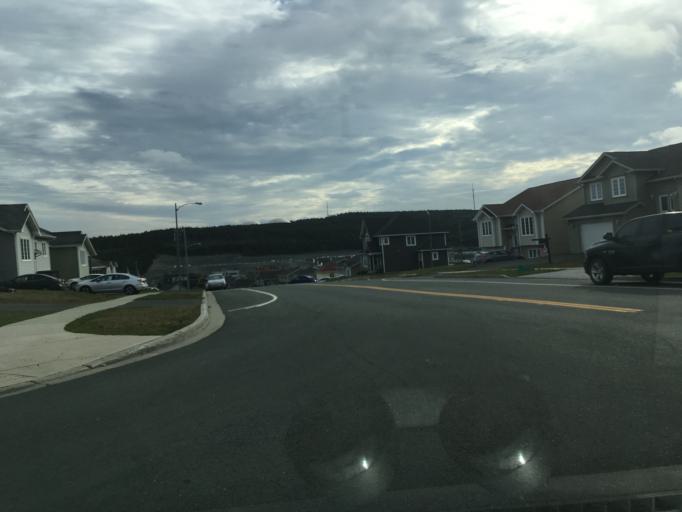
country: CA
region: Newfoundland and Labrador
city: Mount Pearl
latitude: 47.5509
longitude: -52.7893
